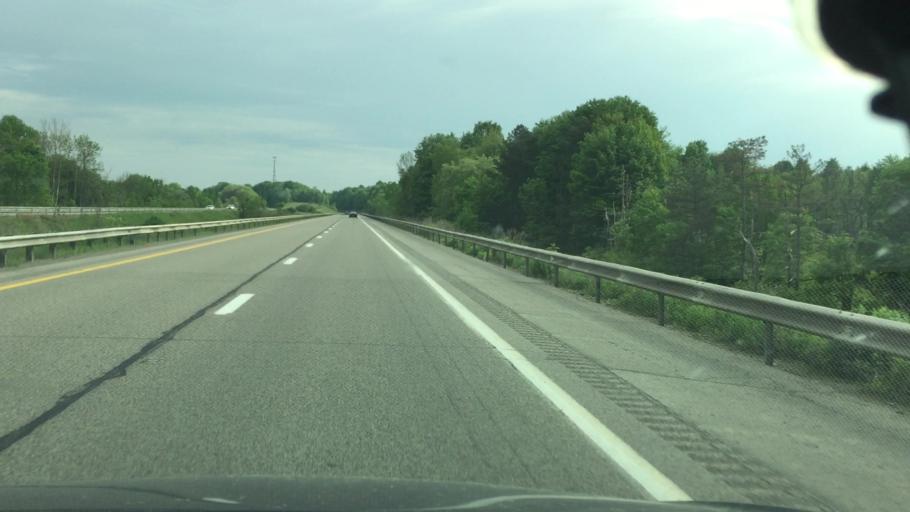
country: US
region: Pennsylvania
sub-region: Mercer County
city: Mercer
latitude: 41.2290
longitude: -80.1627
